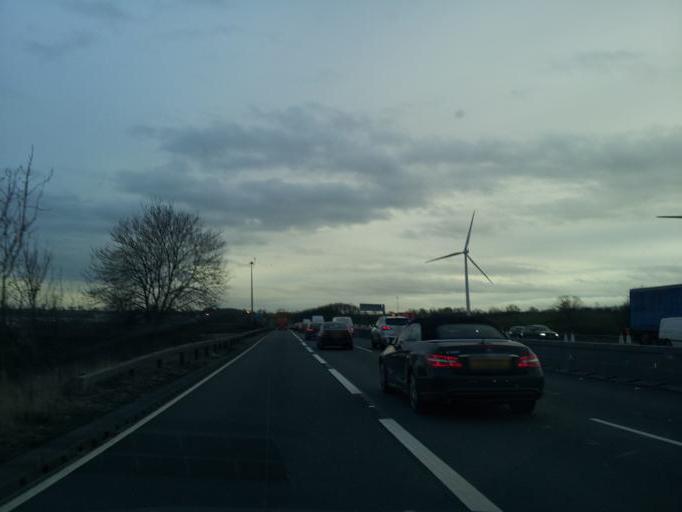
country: GB
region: England
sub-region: Northamptonshire
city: Long Buckby
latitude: 52.3518
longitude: -1.1544
